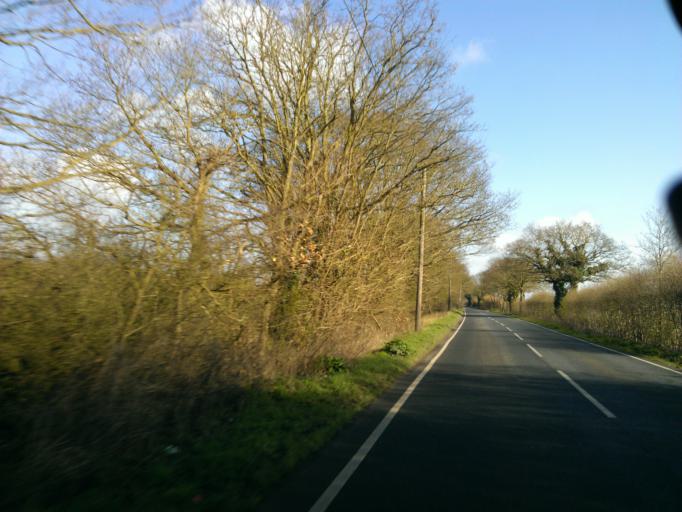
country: GB
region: England
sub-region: Essex
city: Alresford
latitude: 51.8731
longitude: 0.9916
